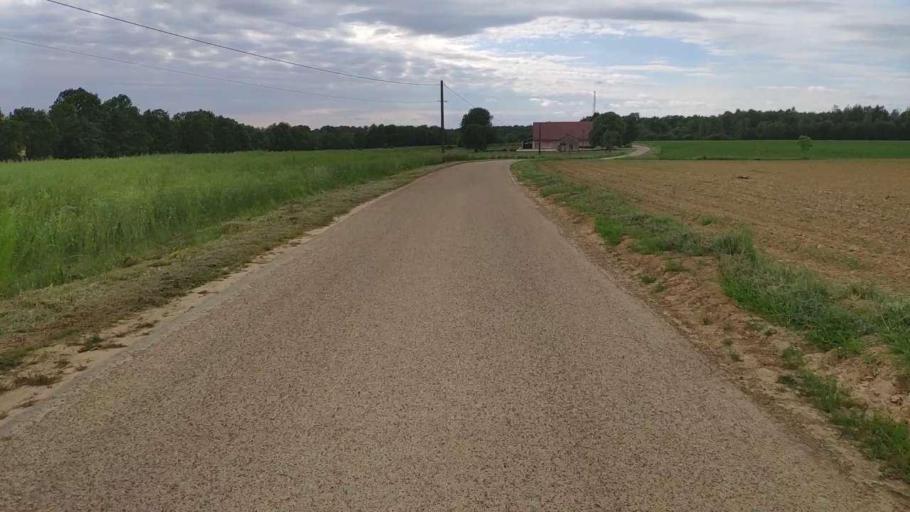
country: FR
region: Franche-Comte
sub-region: Departement du Jura
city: Bletterans
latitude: 46.8000
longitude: 5.5399
